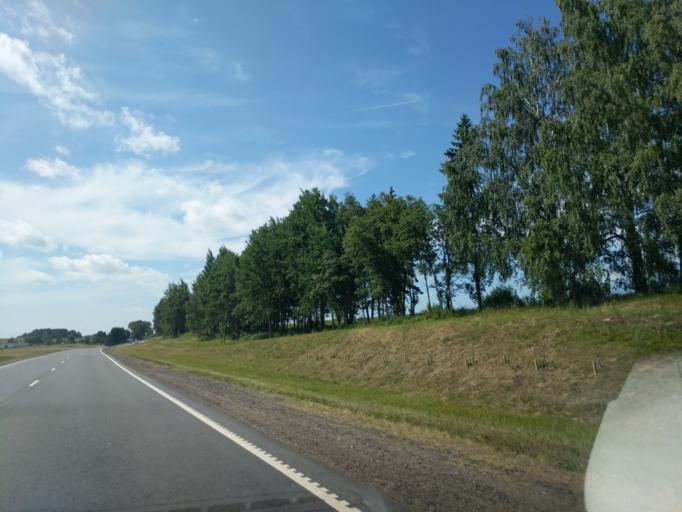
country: BY
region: Minsk
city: Syomkava
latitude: 54.0990
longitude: 27.4899
